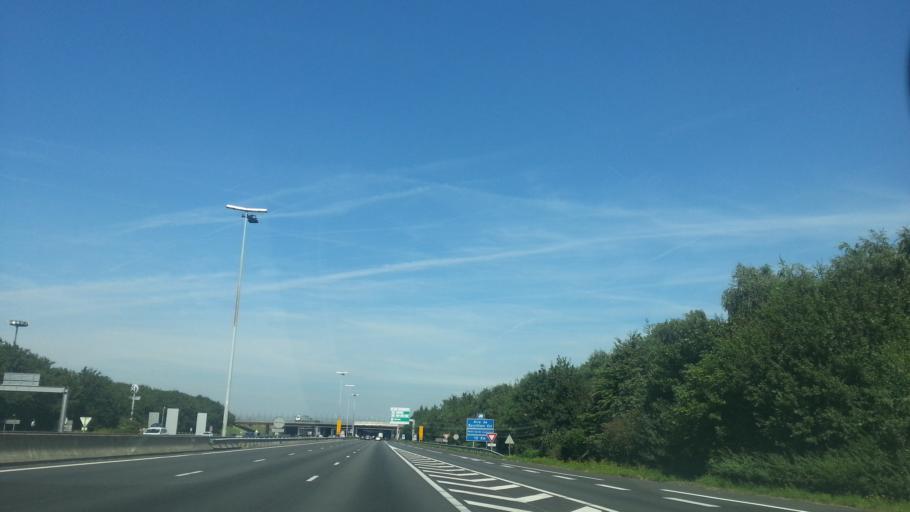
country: FR
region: Ile-de-France
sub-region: Departement du Val-d'Oise
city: Roissy-en-France
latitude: 49.0130
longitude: 2.5303
